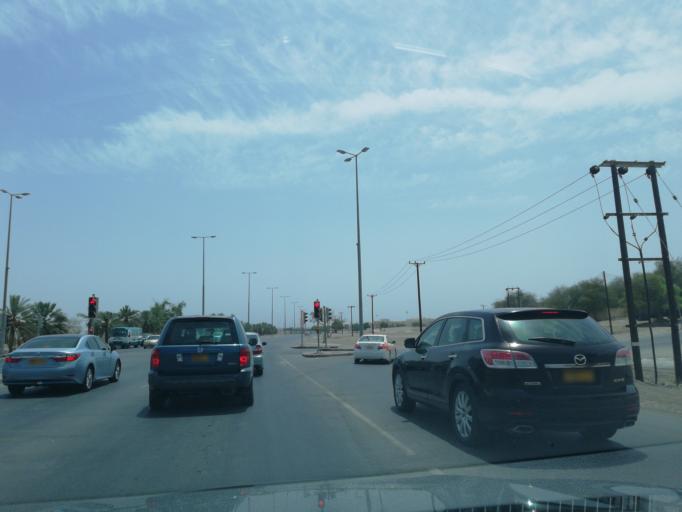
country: OM
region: Muhafazat Masqat
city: As Sib al Jadidah
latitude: 23.6753
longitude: 58.1660
